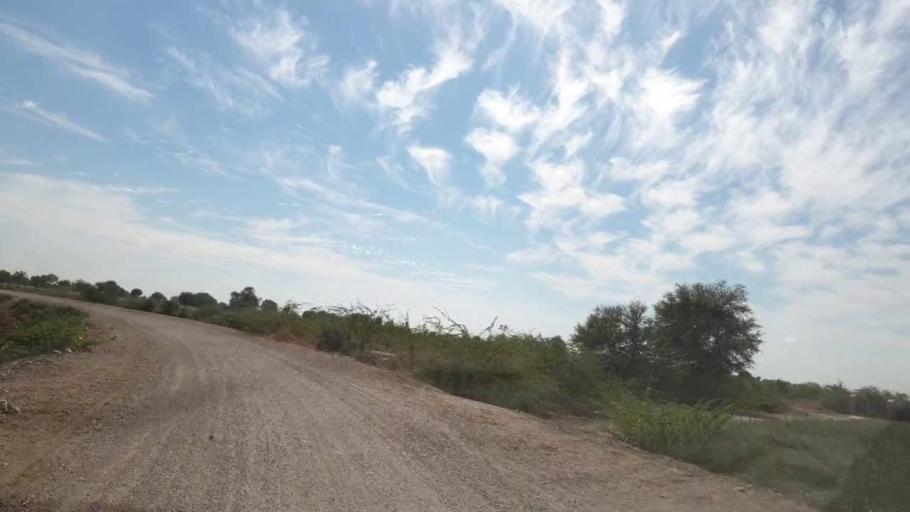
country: PK
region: Sindh
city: Pithoro
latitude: 25.5554
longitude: 69.2979
